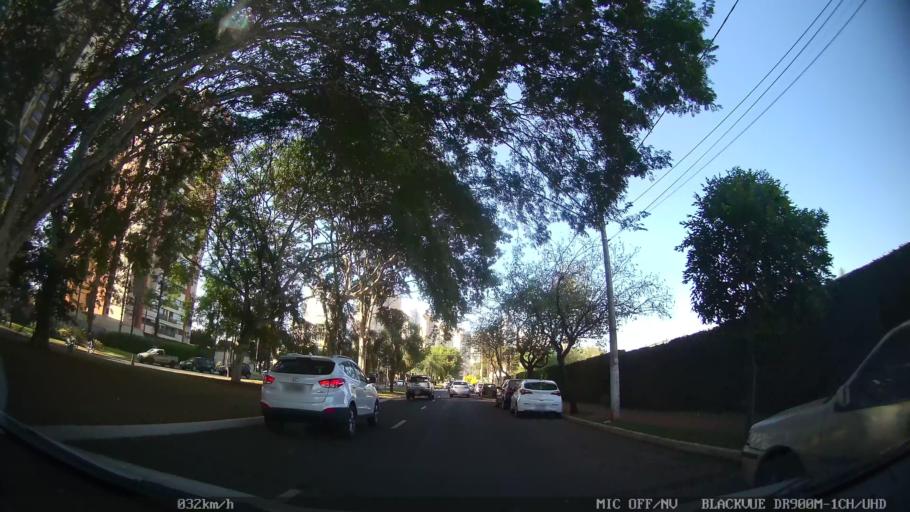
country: BR
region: Sao Paulo
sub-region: Ribeirao Preto
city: Ribeirao Preto
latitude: -21.2094
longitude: -47.8072
